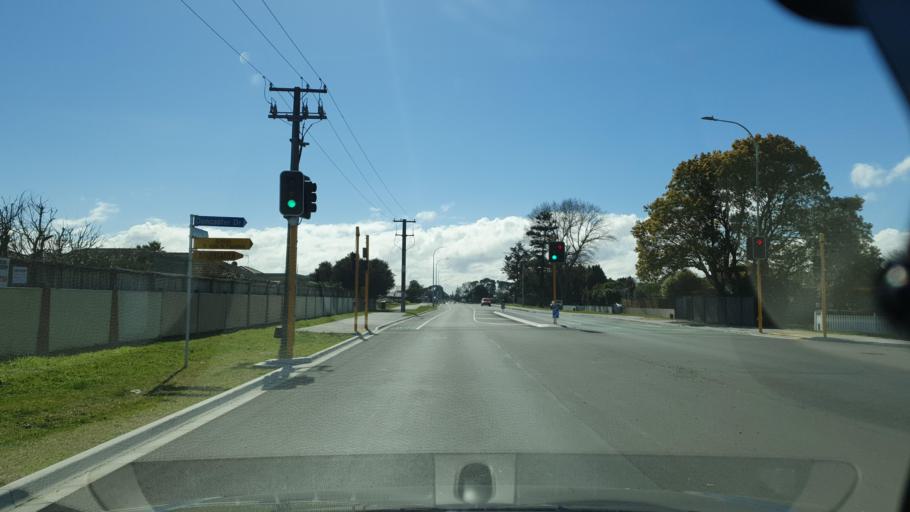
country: NZ
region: Bay of Plenty
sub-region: Tauranga City
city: Tauranga
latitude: -37.7072
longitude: 176.2847
